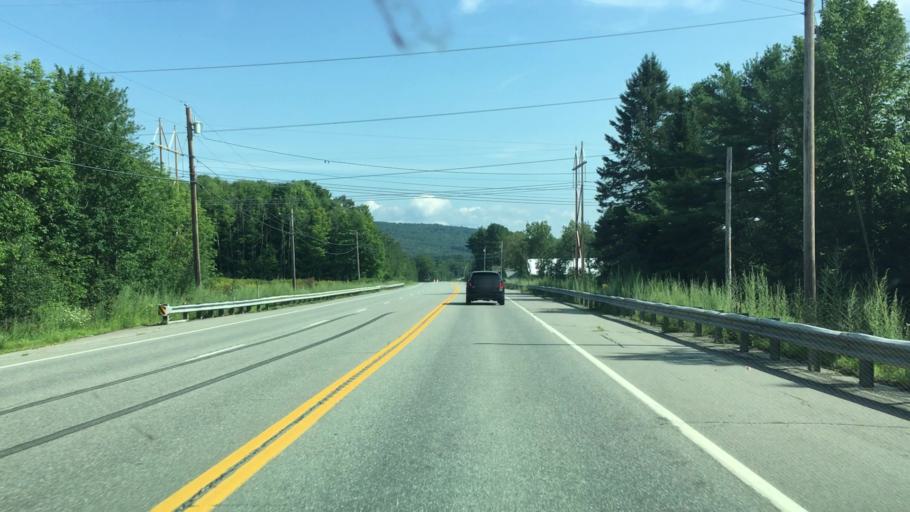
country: US
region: Maine
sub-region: Waldo County
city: Winterport
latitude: 44.6753
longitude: -68.8396
